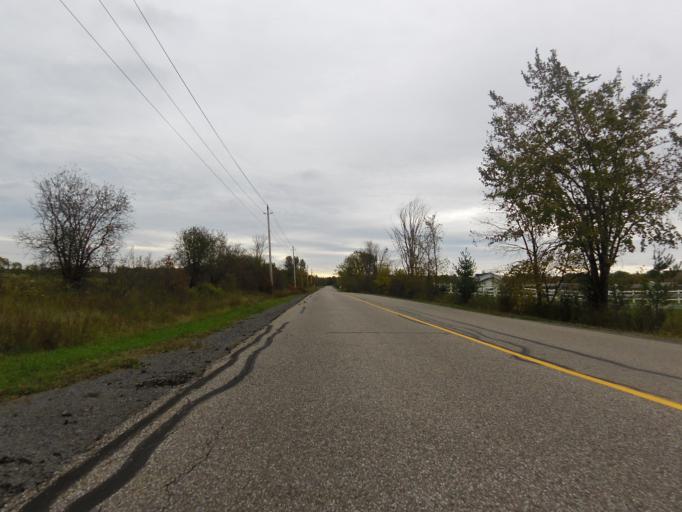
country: CA
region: Ontario
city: Bells Corners
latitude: 45.4022
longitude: -76.0684
